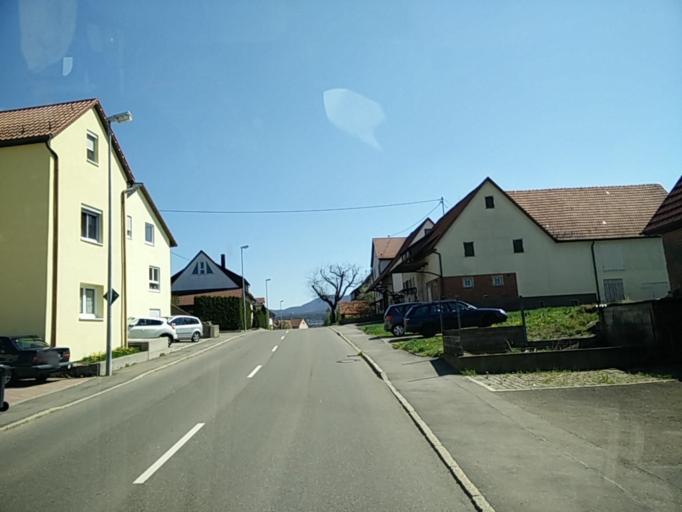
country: DE
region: Baden-Wuerttemberg
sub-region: Tuebingen Region
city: Gomaringen
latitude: 48.4621
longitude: 9.0920
